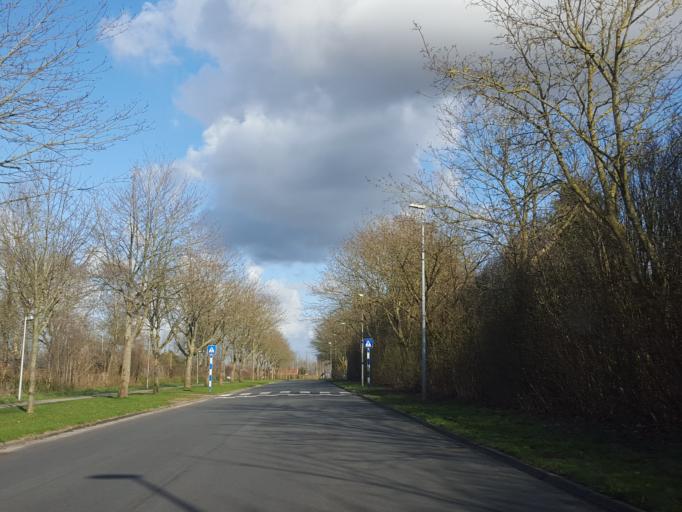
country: DK
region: South Denmark
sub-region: Esbjerg Kommune
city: Bramming
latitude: 55.4765
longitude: 8.7075
